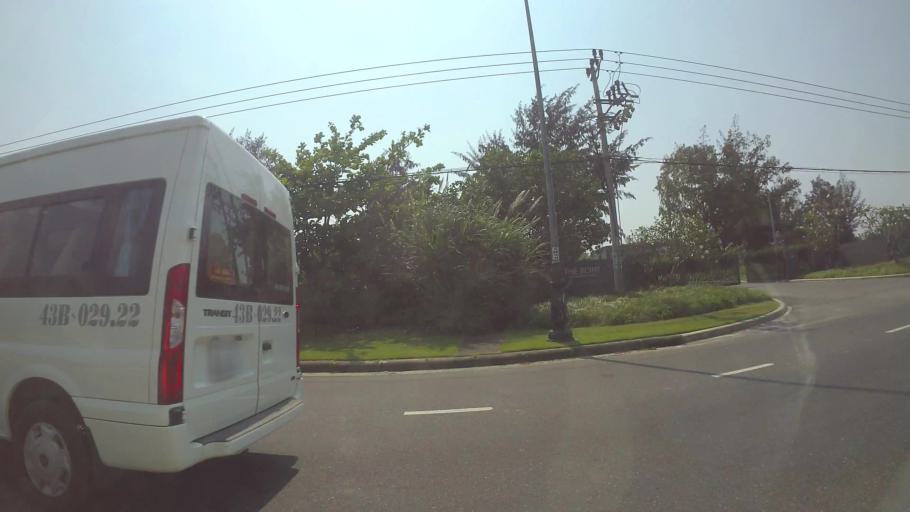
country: VN
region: Da Nang
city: Ngu Hanh Son
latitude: 15.9791
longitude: 108.2768
